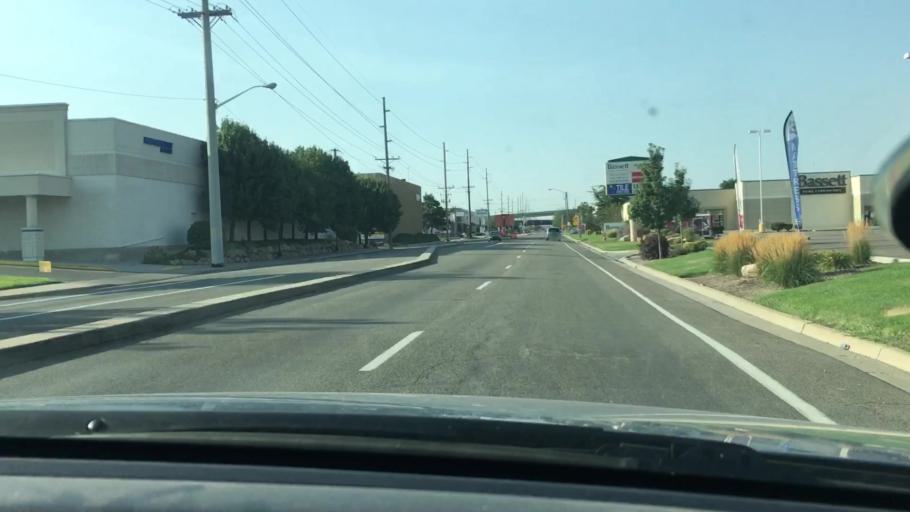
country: US
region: Utah
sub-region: Salt Lake County
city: South Salt Lake
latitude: 40.7248
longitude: -111.8998
